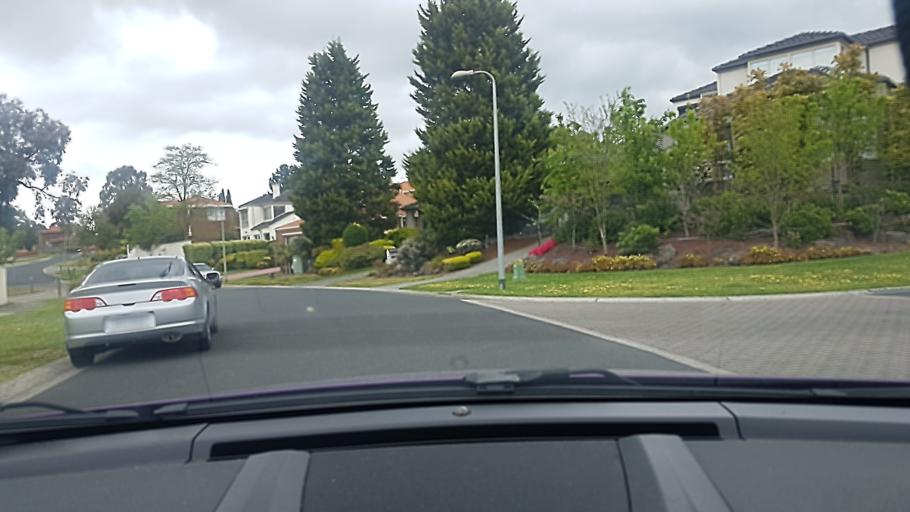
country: AU
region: Victoria
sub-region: Manningham
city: Doncaster East
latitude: -37.7612
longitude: 145.1615
